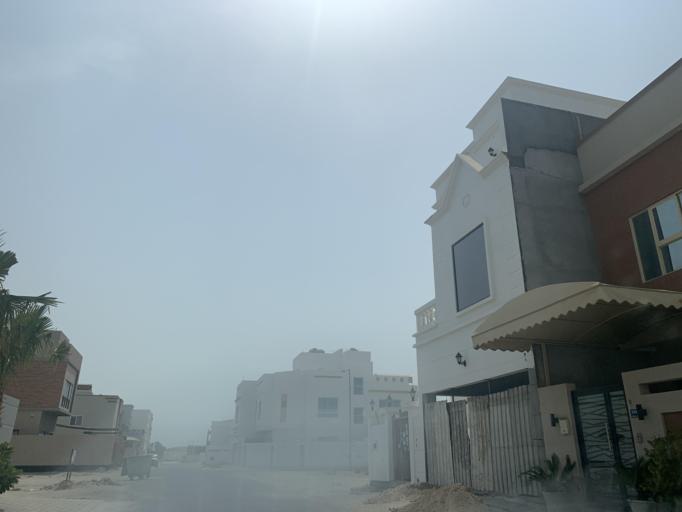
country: BH
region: Manama
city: Jidd Hafs
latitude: 26.2018
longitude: 50.4687
